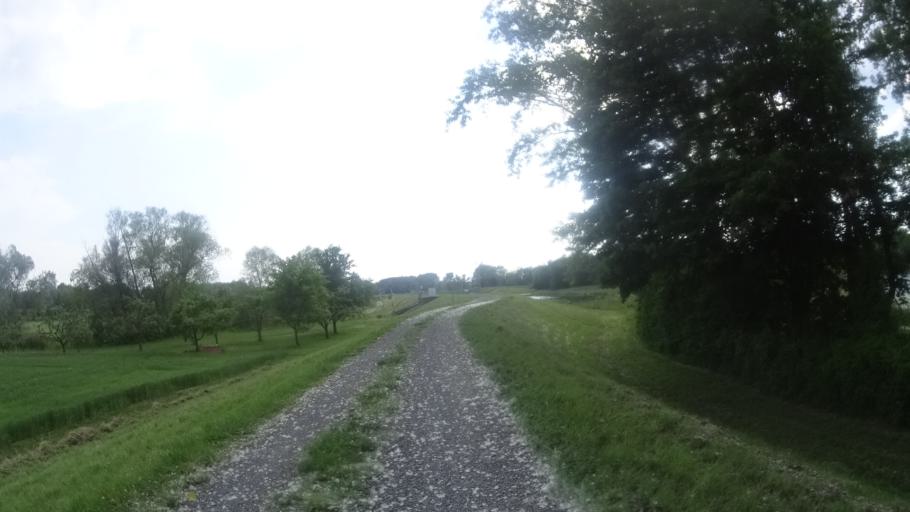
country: DE
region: Baden-Wuerttemberg
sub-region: Karlsruhe Region
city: Hugelsheim
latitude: 48.7982
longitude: 8.0893
